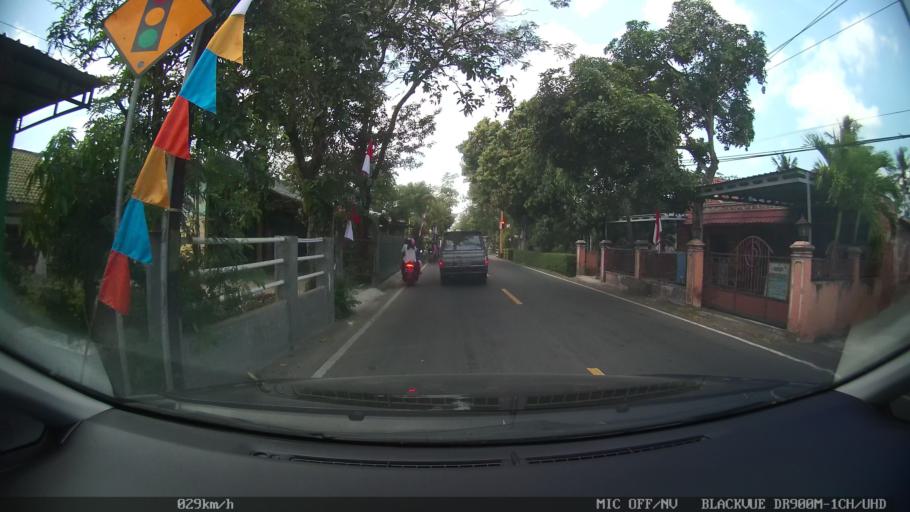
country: ID
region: Daerah Istimewa Yogyakarta
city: Bantul
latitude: -7.9076
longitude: 110.3441
